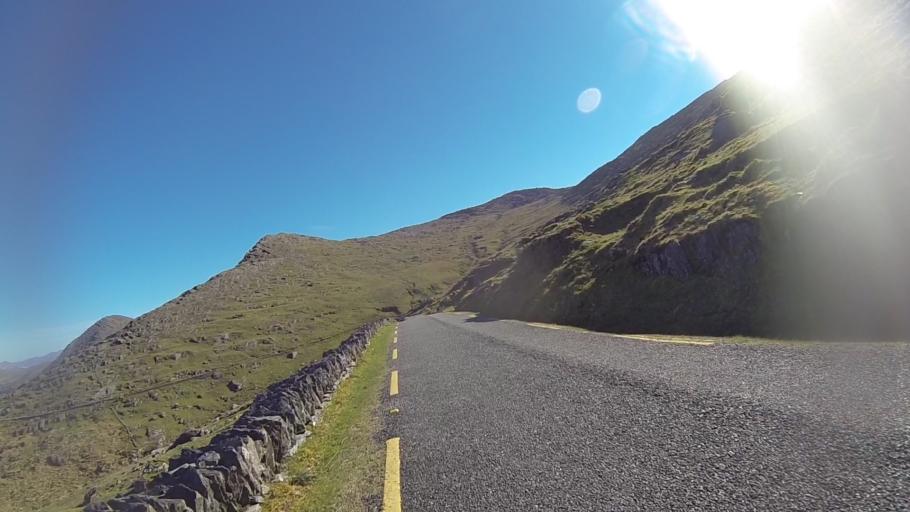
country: IE
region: Munster
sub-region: Ciarrai
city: Kenmare
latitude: 51.7280
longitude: -9.7558
